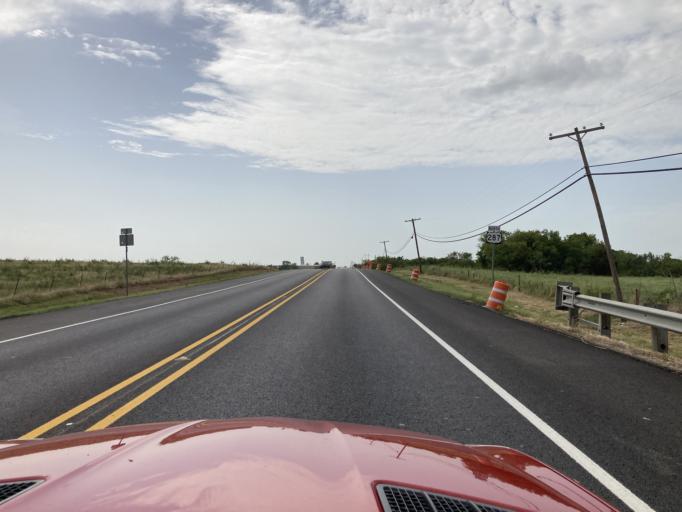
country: US
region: Texas
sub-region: Navarro County
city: Corsicana
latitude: 32.0567
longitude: -96.4284
